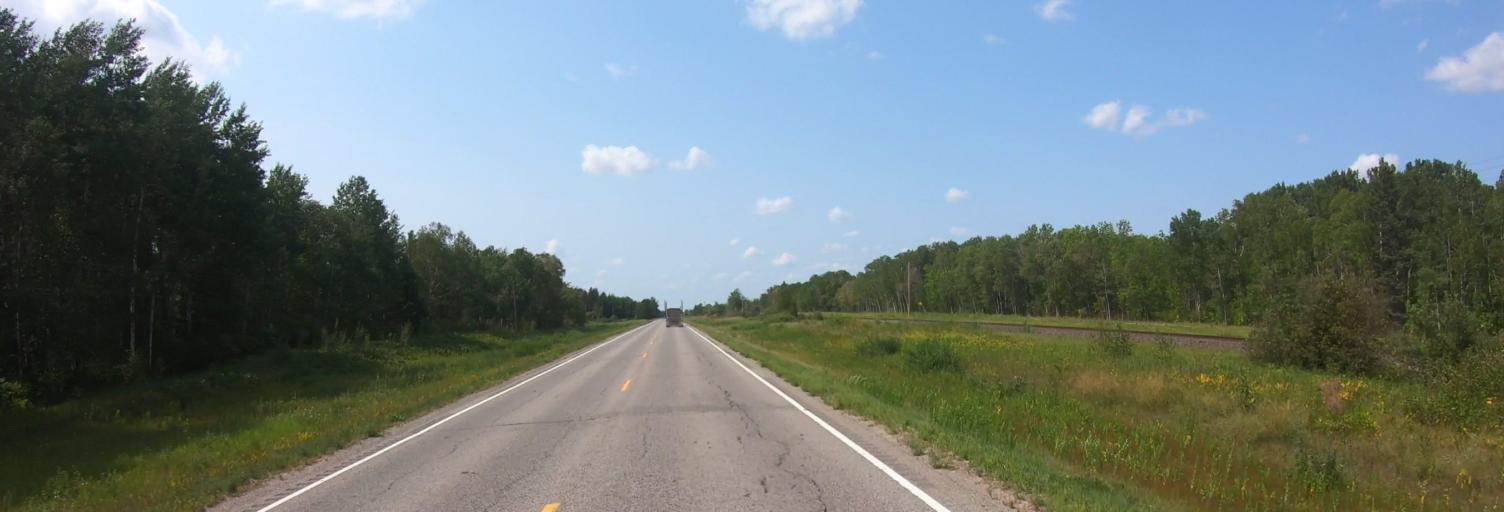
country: US
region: Minnesota
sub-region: Roseau County
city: Warroad
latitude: 48.8160
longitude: -95.1308
